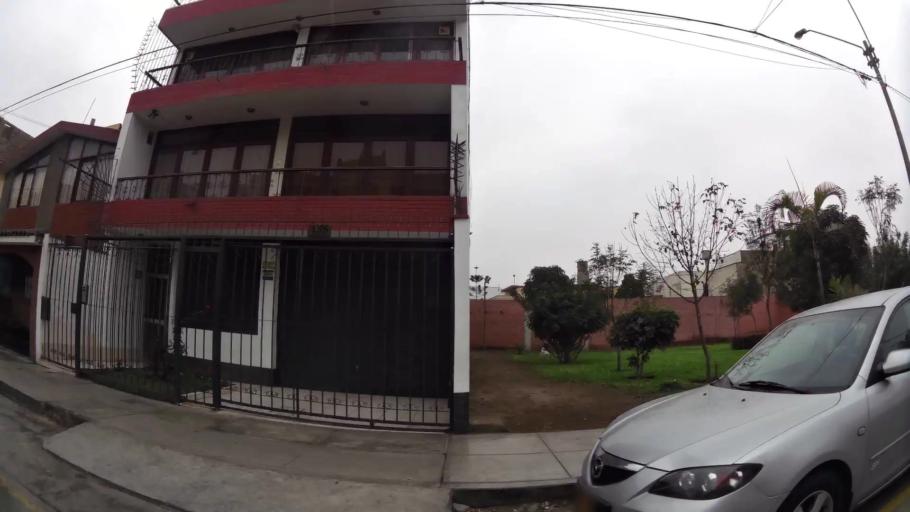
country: PE
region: Lima
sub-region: Lima
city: San Luis
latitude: -12.1057
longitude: -77.0003
